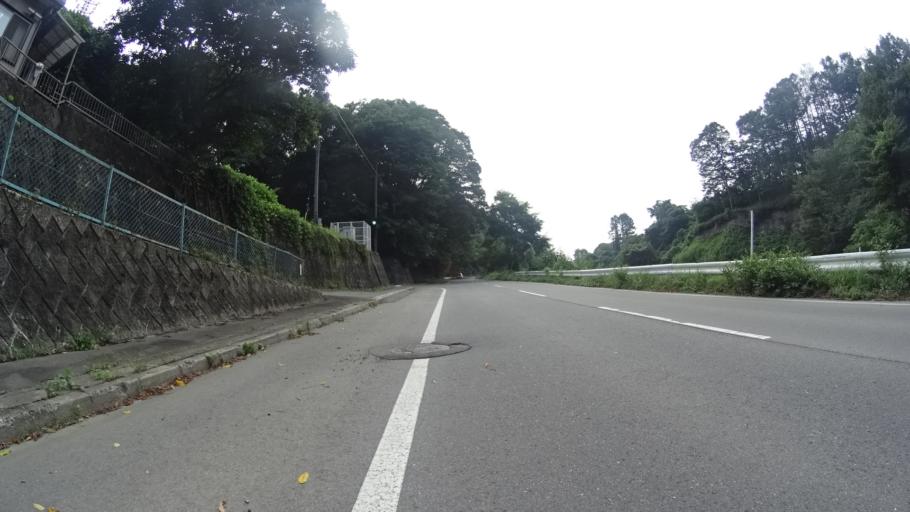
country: JP
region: Nagano
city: Chino
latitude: 35.9738
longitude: 138.1801
